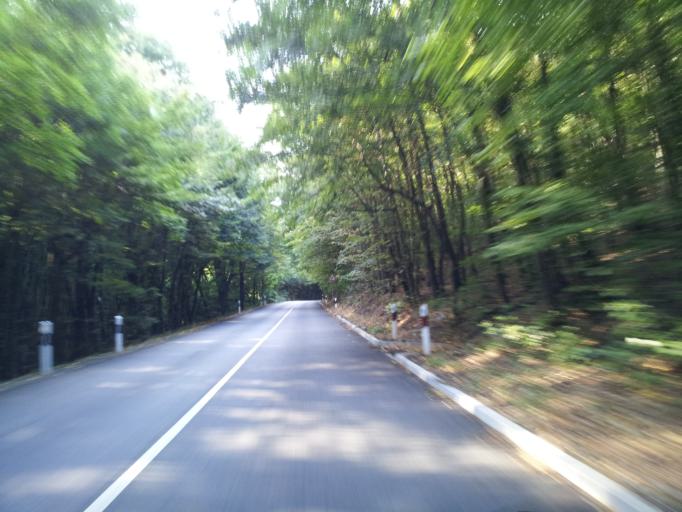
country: HU
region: Pest
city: Nagymaros
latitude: 47.8358
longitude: 18.9583
